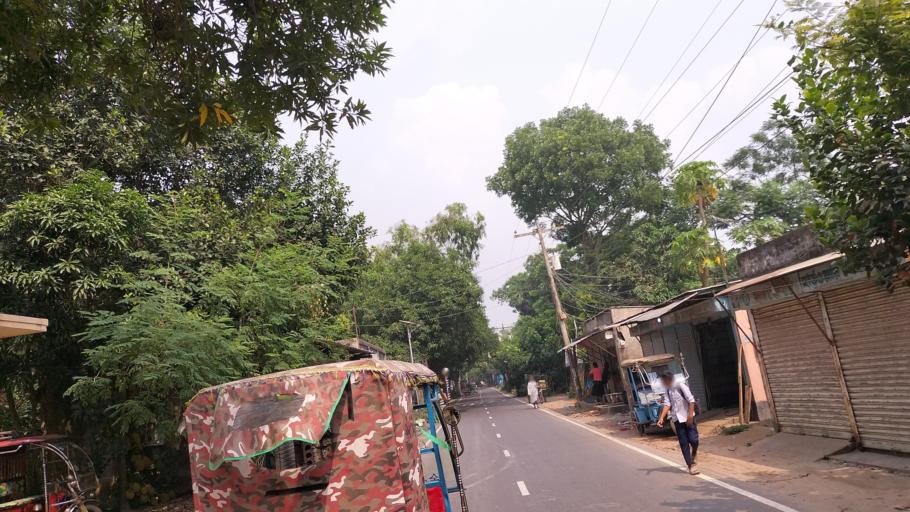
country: BD
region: Dhaka
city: Azimpur
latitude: 23.6972
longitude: 90.2949
